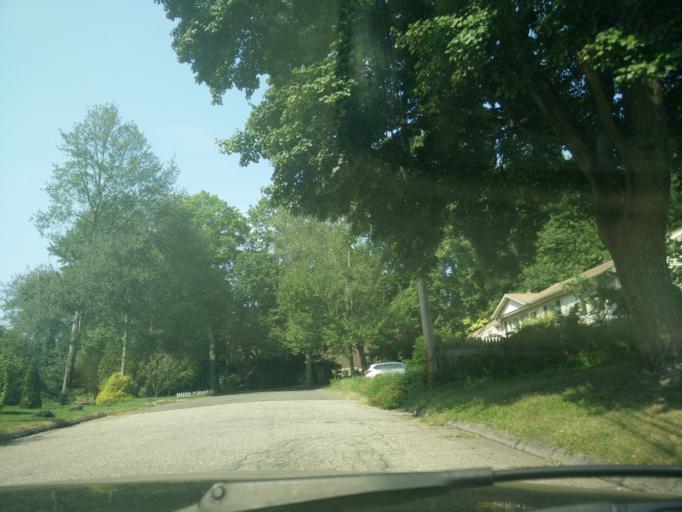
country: US
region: Connecticut
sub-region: Fairfield County
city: Bridgeport
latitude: 41.1841
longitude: -73.2323
